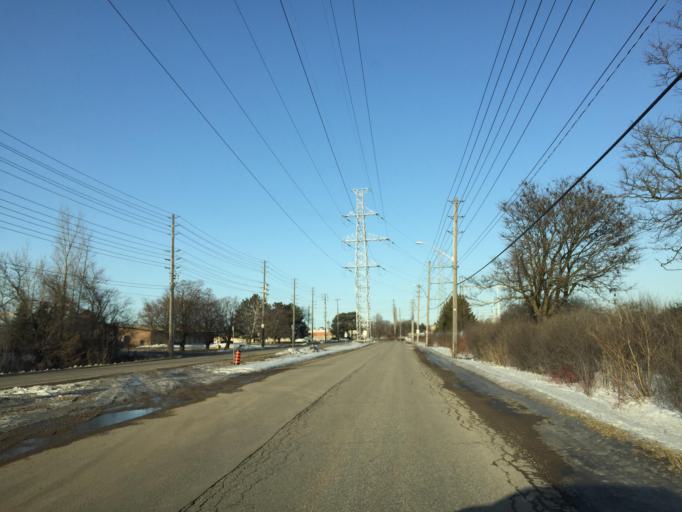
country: CA
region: Ontario
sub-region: Wellington County
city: Guelph
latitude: 43.5518
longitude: -80.2866
